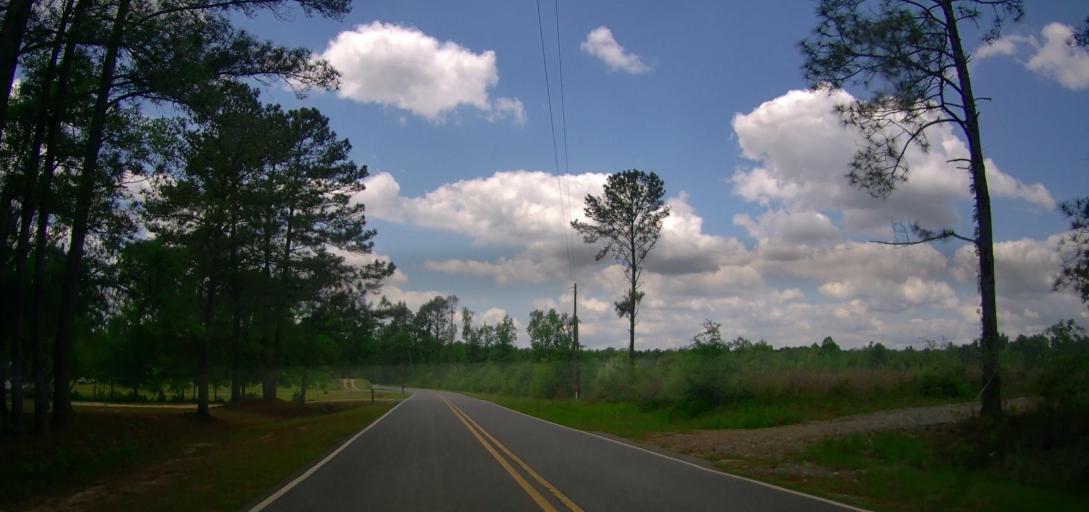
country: US
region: Georgia
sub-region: Laurens County
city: East Dublin
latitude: 32.6196
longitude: -82.8201
